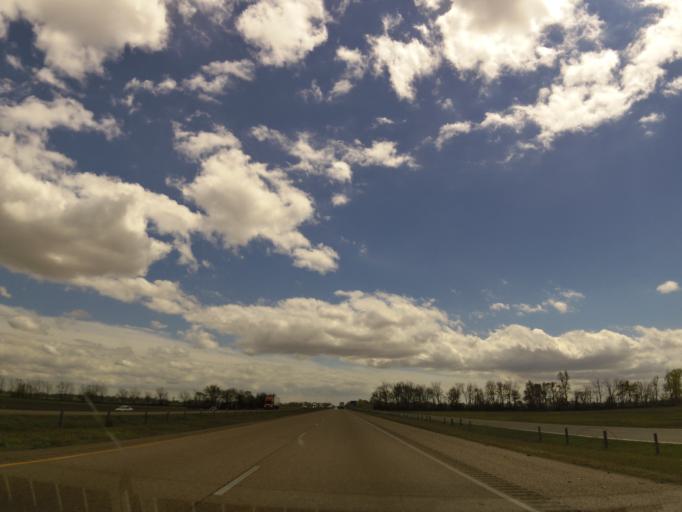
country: US
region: Arkansas
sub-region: Crittenden County
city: Marion
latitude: 35.2885
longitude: -90.2418
